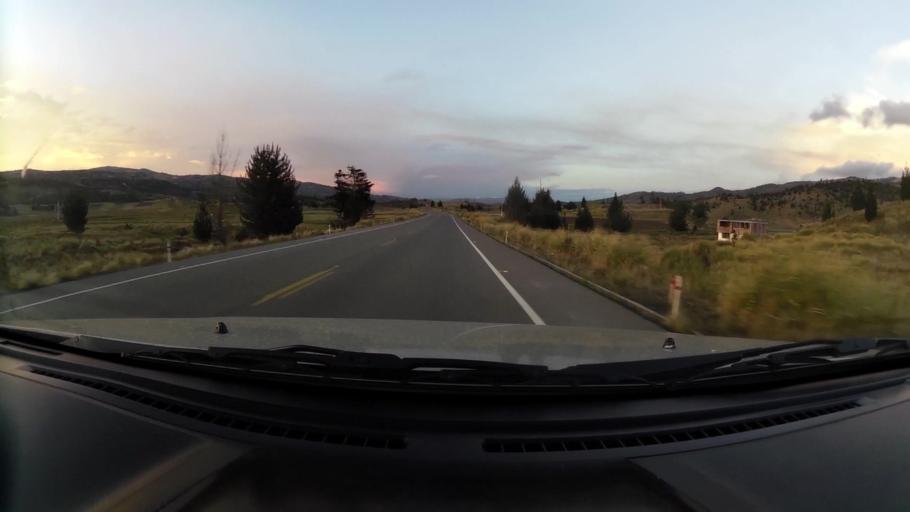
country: EC
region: Chimborazo
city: Alausi
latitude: -2.0062
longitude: -78.7281
